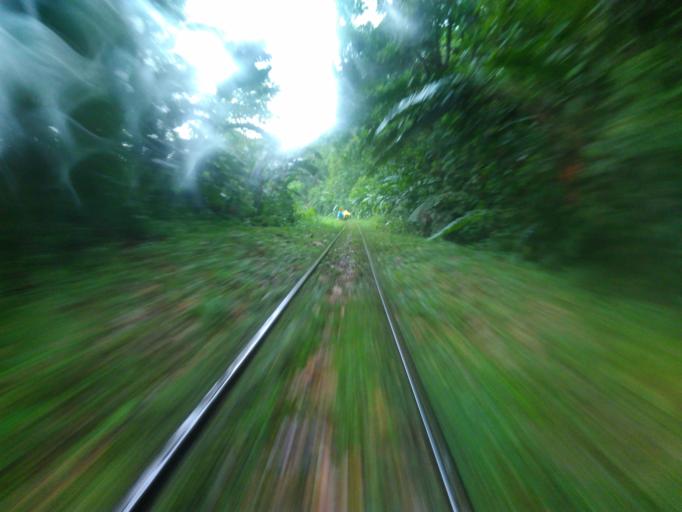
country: CO
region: Valle del Cauca
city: Buenaventura
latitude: 3.8465
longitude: -76.8643
